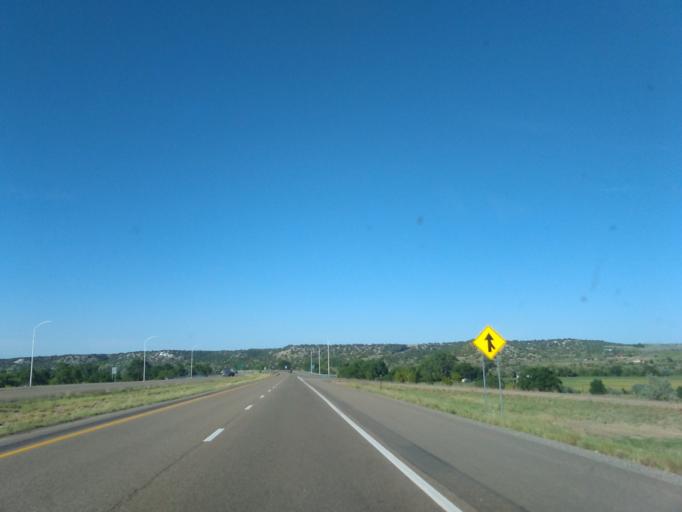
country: US
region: New Mexico
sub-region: San Miguel County
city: Las Vegas
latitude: 35.5702
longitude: -105.2185
